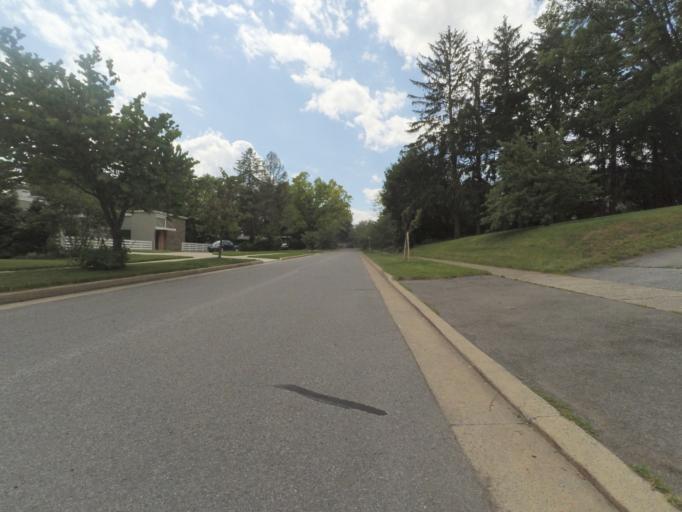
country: US
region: Pennsylvania
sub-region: Centre County
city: State College
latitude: 40.7835
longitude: -77.8675
